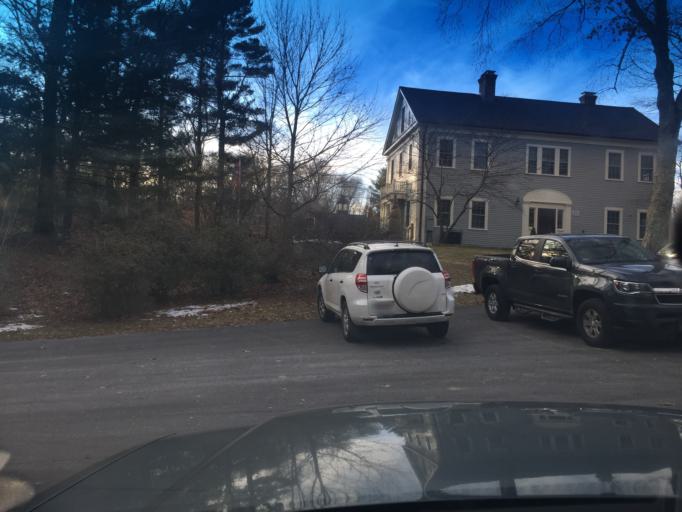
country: US
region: Massachusetts
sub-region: Middlesex County
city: Sherborn
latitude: 42.2453
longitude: -71.3728
